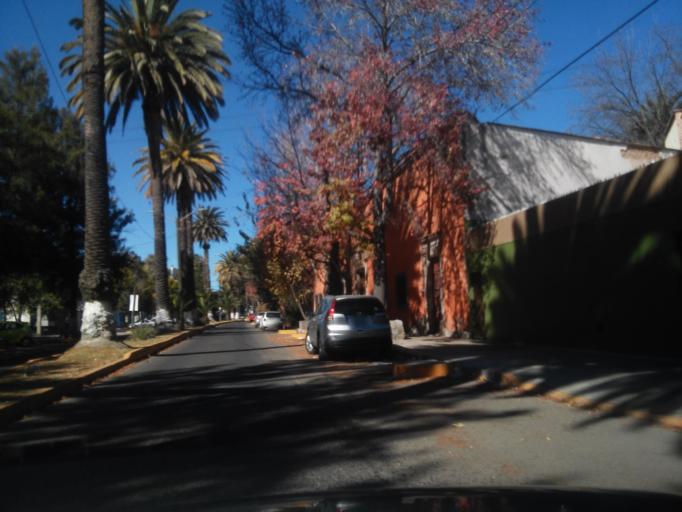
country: MX
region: Durango
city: Victoria de Durango
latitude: 24.0224
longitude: -104.6777
